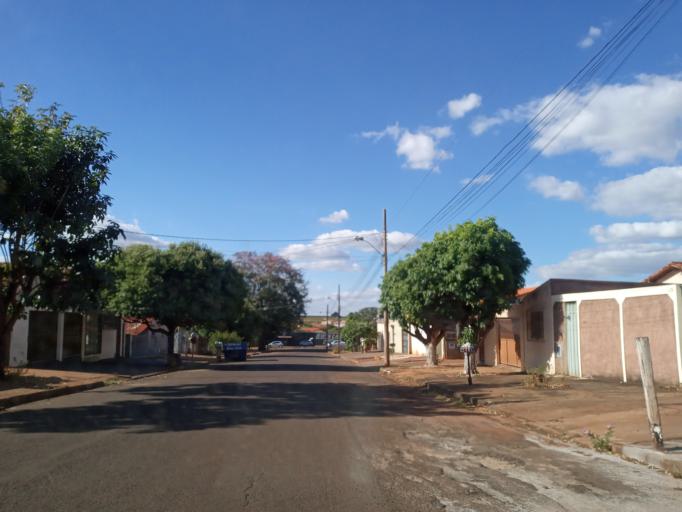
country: BR
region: Minas Gerais
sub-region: Ituiutaba
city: Ituiutaba
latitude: -18.9617
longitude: -49.4529
